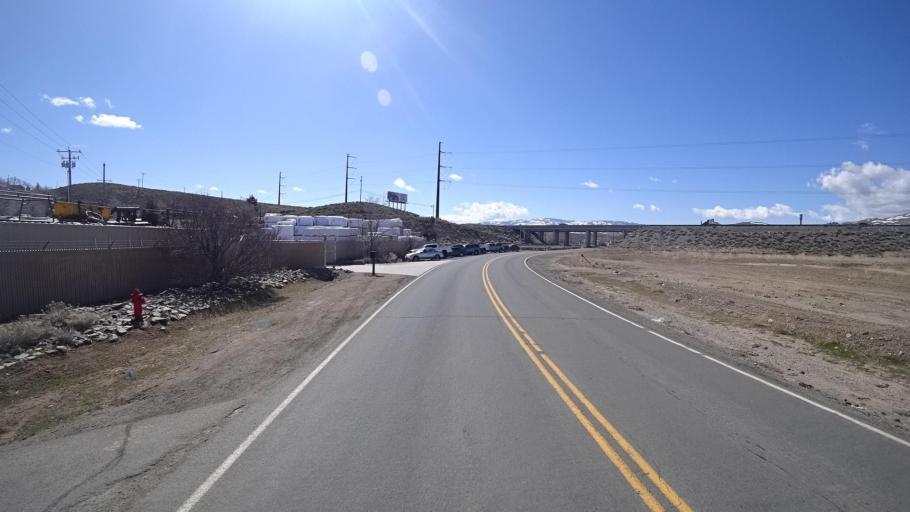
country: US
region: Nevada
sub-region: Washoe County
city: Golden Valley
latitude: 39.5883
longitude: -119.8228
